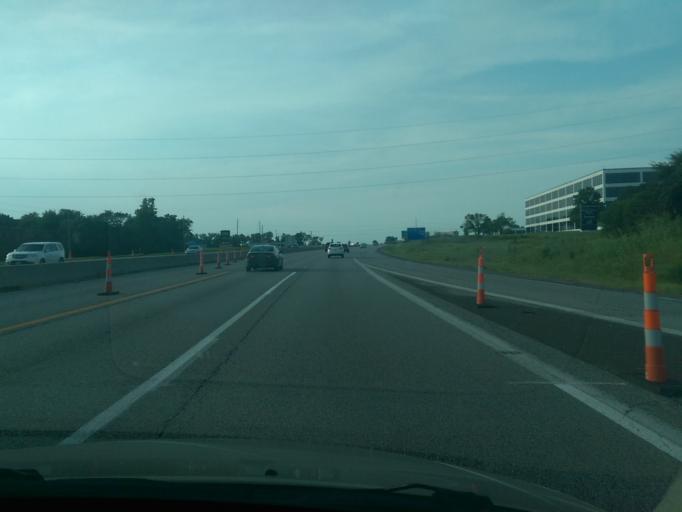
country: US
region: Missouri
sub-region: Platte County
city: Weatherby Lake
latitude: 39.2987
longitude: -94.6859
